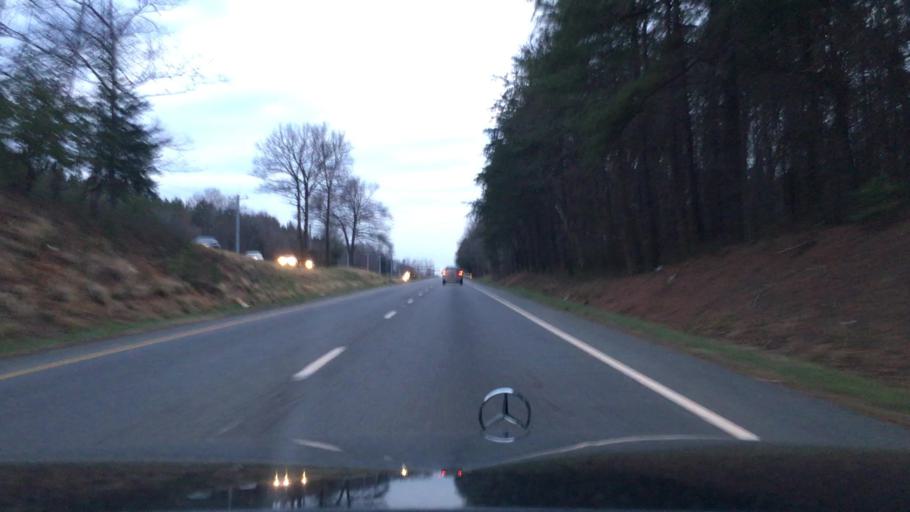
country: US
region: Virginia
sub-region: Greene County
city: Ruckersville
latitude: 38.1799
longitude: -78.4044
